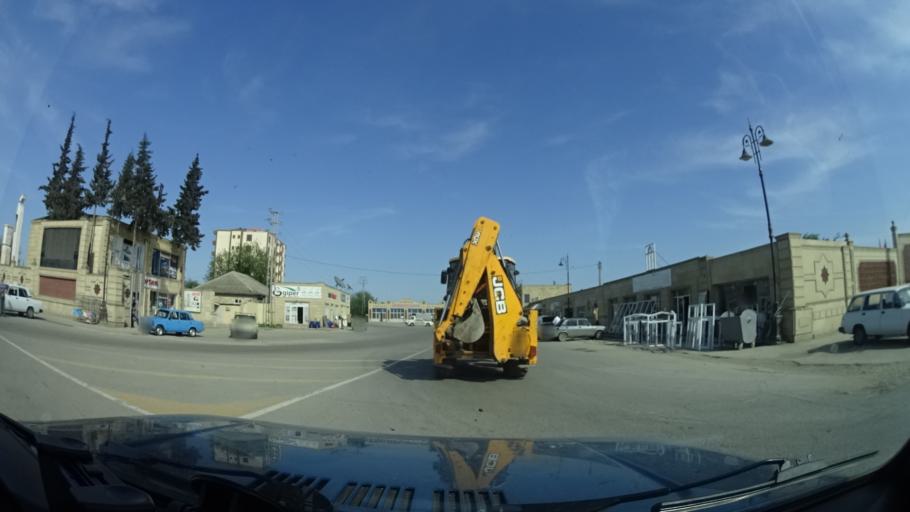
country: AZ
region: Salyan
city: Salyan
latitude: 39.5883
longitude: 48.9744
